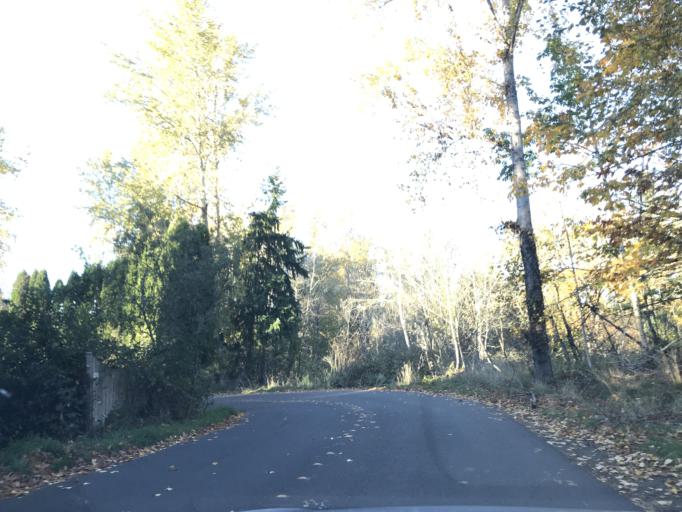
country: US
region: Washington
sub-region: Whatcom County
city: Geneva
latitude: 48.7558
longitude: -122.4208
